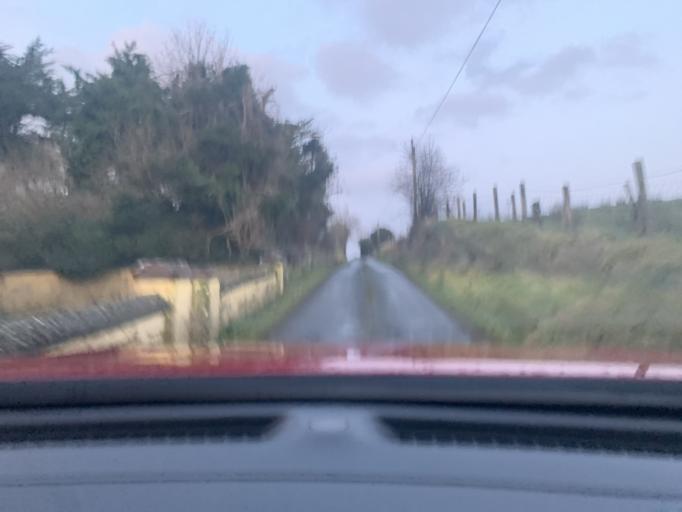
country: IE
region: Connaught
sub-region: Sligo
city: Ballymote
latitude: 54.0731
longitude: -8.3898
